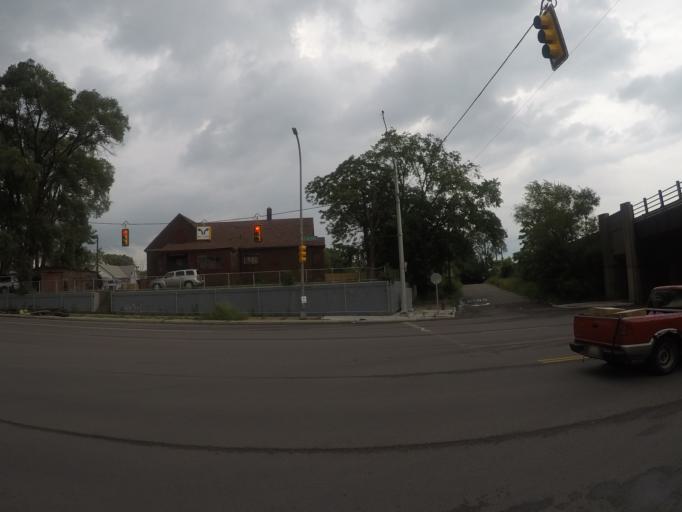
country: US
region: Michigan
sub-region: Wayne County
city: River Rouge
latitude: 42.3243
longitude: -83.1155
